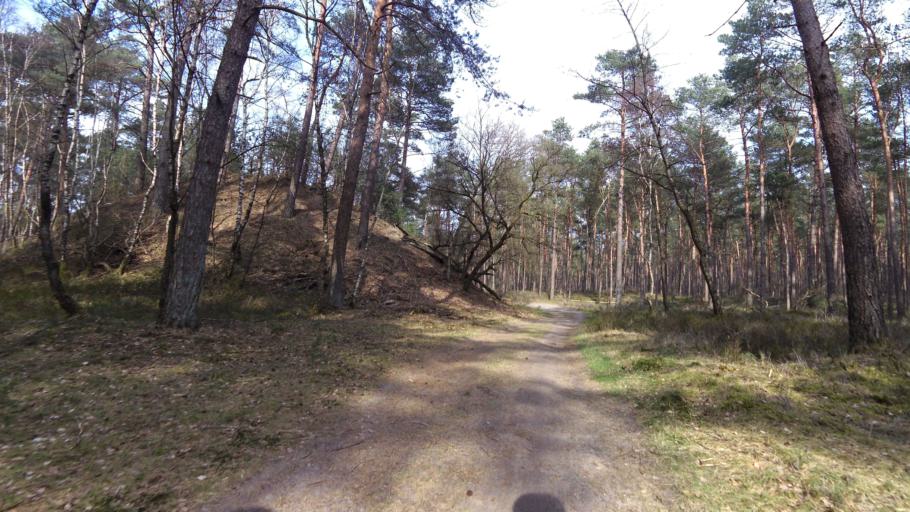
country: NL
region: Gelderland
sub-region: Gemeente Ede
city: Otterlo
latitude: 52.0804
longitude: 5.7441
